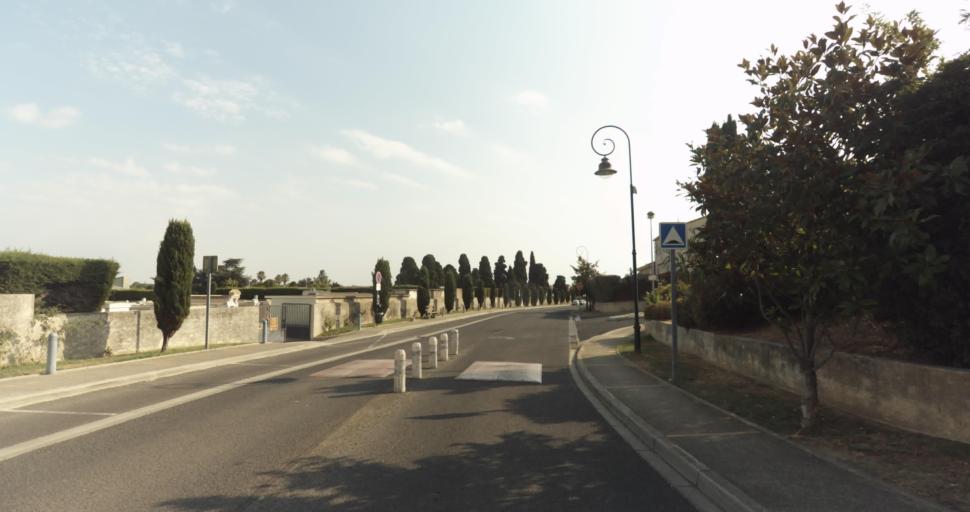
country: FR
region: Languedoc-Roussillon
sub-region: Departement des Pyrenees-Orientales
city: Latour-Bas-Elne
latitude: 42.6155
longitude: 2.9976
